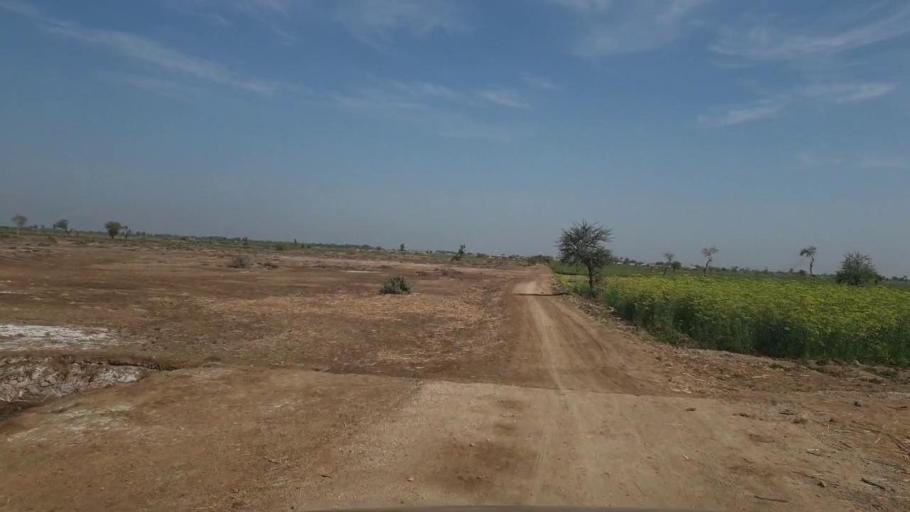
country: PK
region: Sindh
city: Samaro
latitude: 25.3600
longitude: 69.2668
